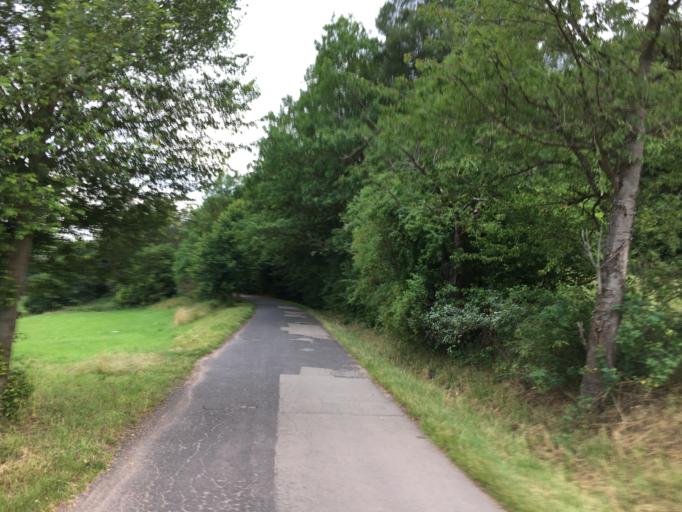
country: DE
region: Thuringia
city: Schmalkalden
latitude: 50.7480
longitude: 10.4662
